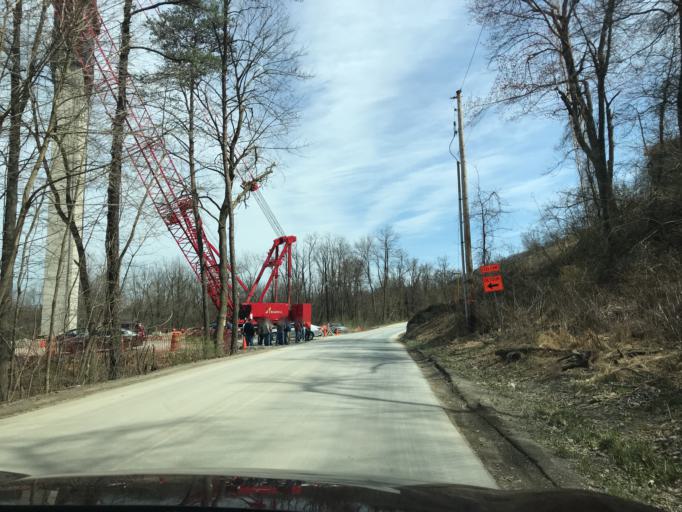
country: US
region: Pennsylvania
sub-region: Northumberland County
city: Northumberland
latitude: 40.8996
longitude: -76.8406
